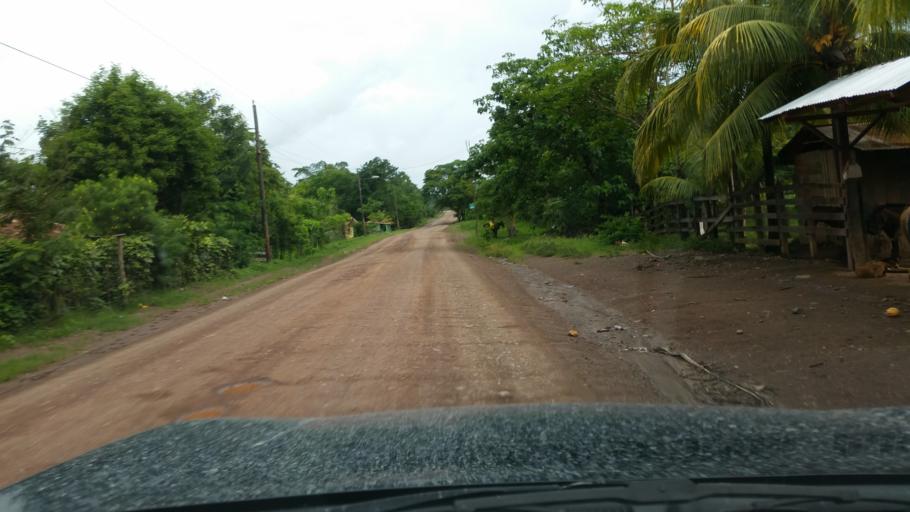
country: NI
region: Atlantico Norte (RAAN)
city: Siuna
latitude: 13.4912
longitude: -84.8446
